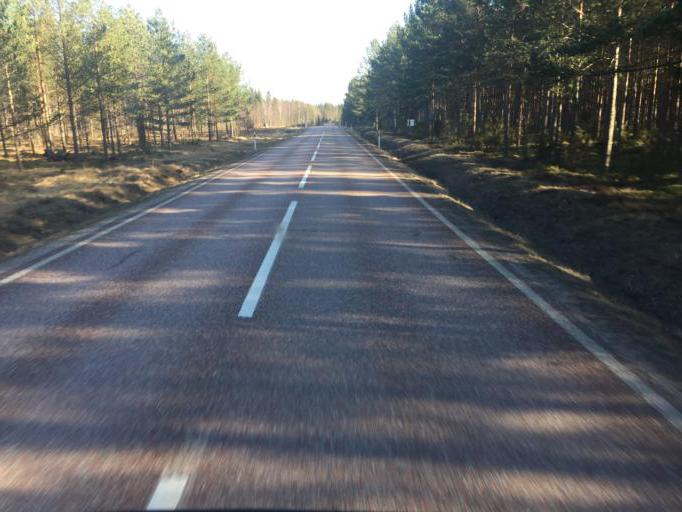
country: SE
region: Dalarna
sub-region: Vansbro Kommun
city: Jarna
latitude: 60.5163
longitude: 14.4550
